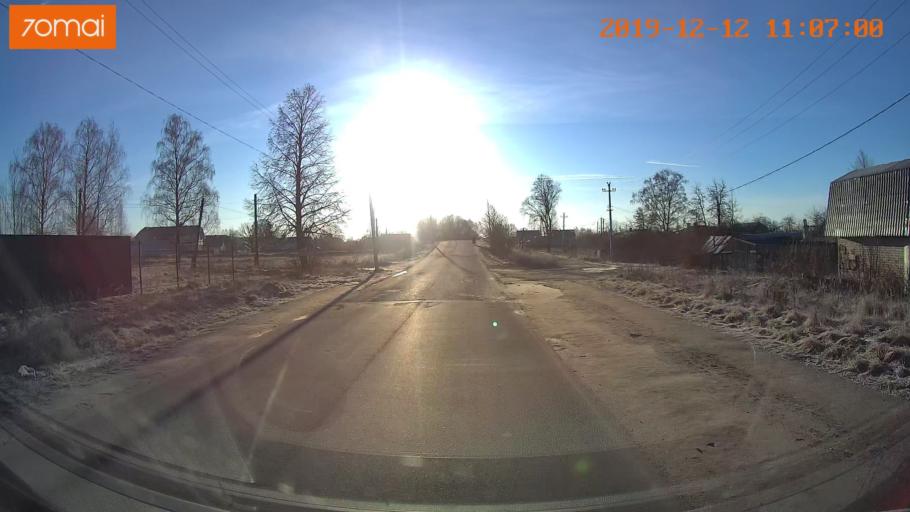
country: RU
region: Ivanovo
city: Kokhma
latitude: 56.9399
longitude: 41.0886
